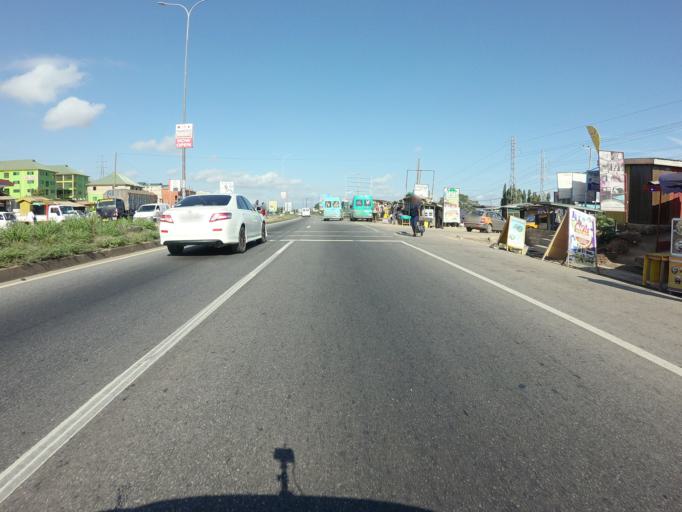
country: GH
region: Greater Accra
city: Gbawe
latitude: 5.5521
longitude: -0.3583
